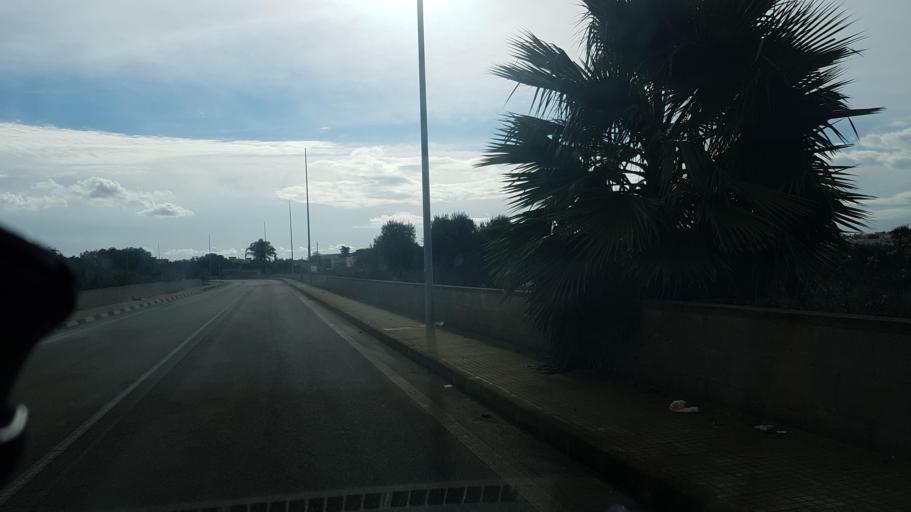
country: IT
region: Apulia
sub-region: Provincia di Brindisi
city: San Vito dei Normanni
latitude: 40.6635
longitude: 17.7143
